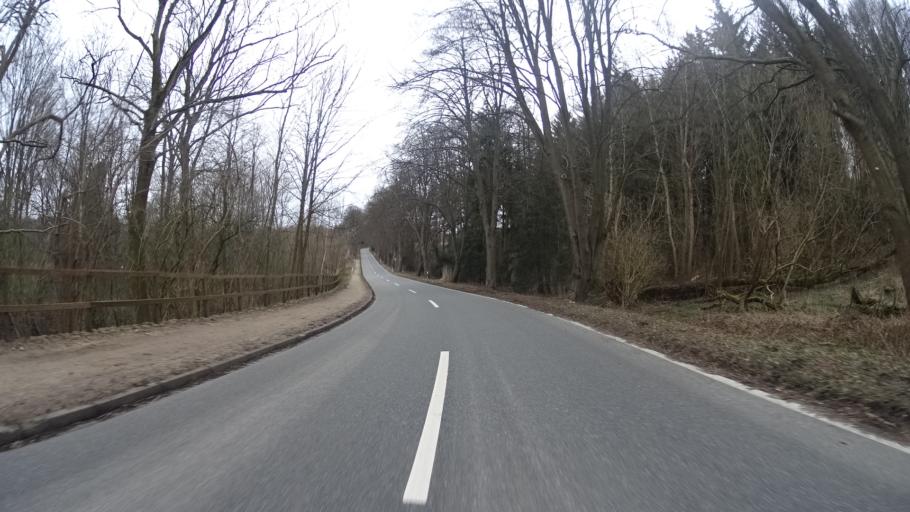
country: DE
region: Schleswig-Holstein
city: Grebin
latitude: 54.1743
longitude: 10.5219
